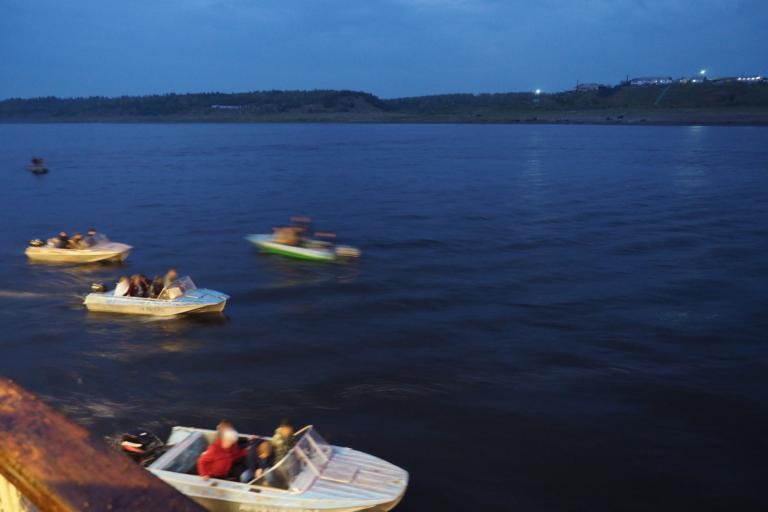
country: RU
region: Krasnoyarskiy
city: Dudinka
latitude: 68.6780
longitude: 86.2628
